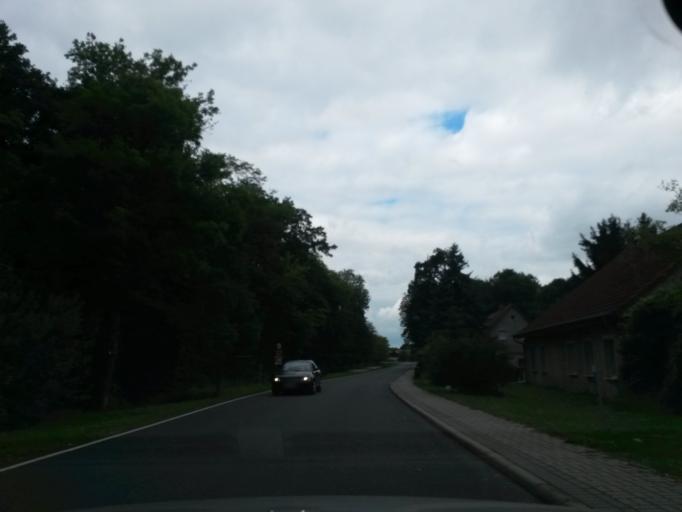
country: DE
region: Brandenburg
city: Gerswalde
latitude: 53.1563
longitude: 13.8480
